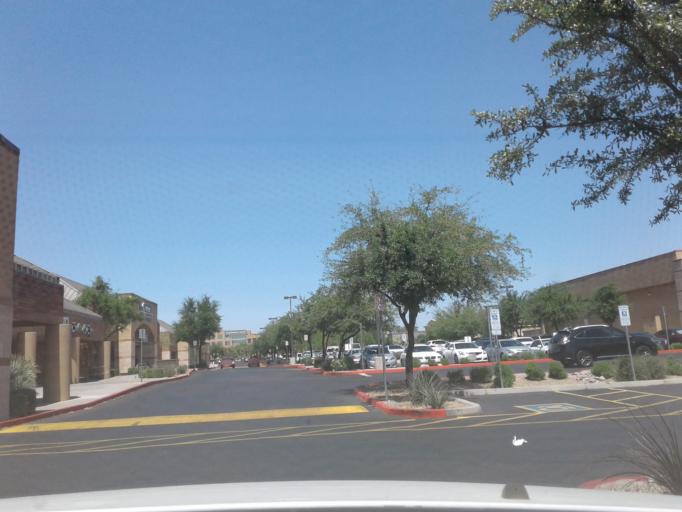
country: US
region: Arizona
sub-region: Maricopa County
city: Paradise Valley
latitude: 33.6158
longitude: -111.9270
